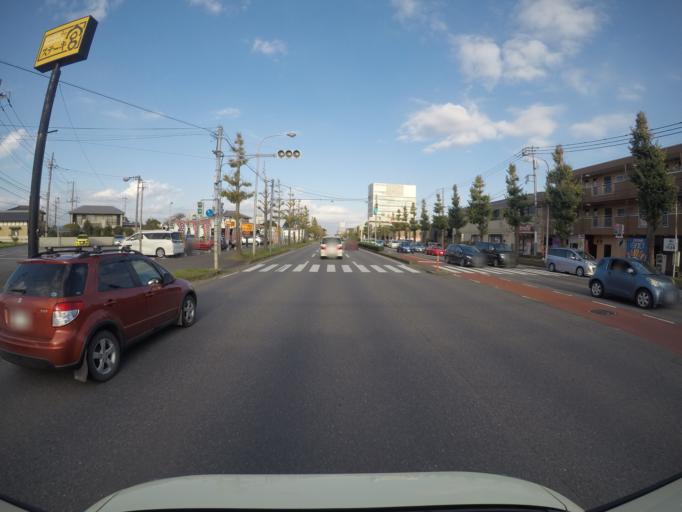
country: JP
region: Ibaraki
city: Naka
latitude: 36.0737
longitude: 140.0986
